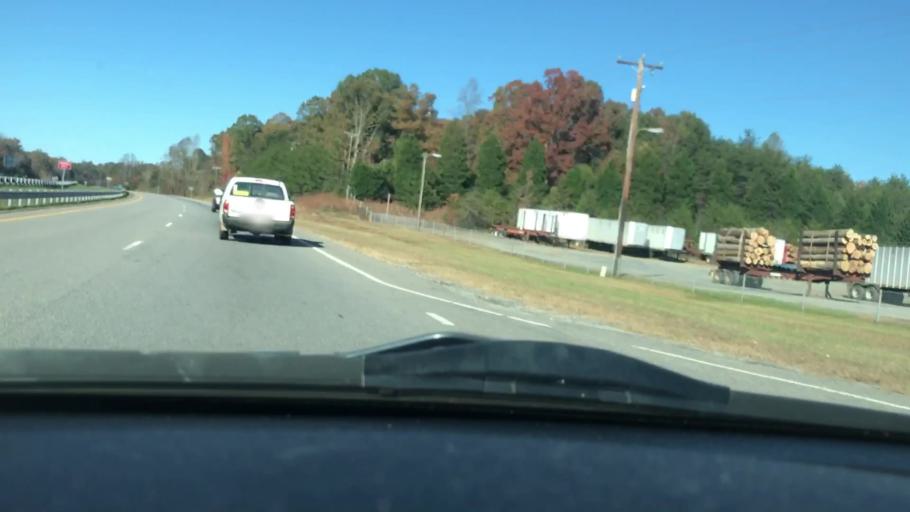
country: US
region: North Carolina
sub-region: Rockingham County
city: Stoneville
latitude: 36.4799
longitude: -79.9239
